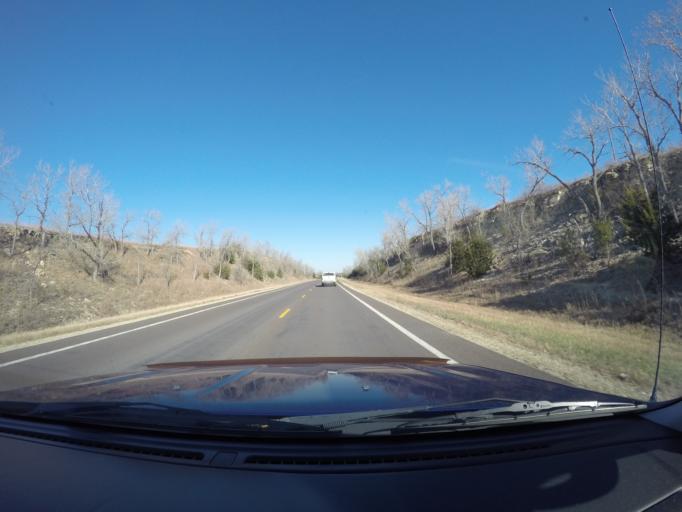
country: US
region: Kansas
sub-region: Marshall County
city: Blue Rapids
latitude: 39.4867
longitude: -96.7553
